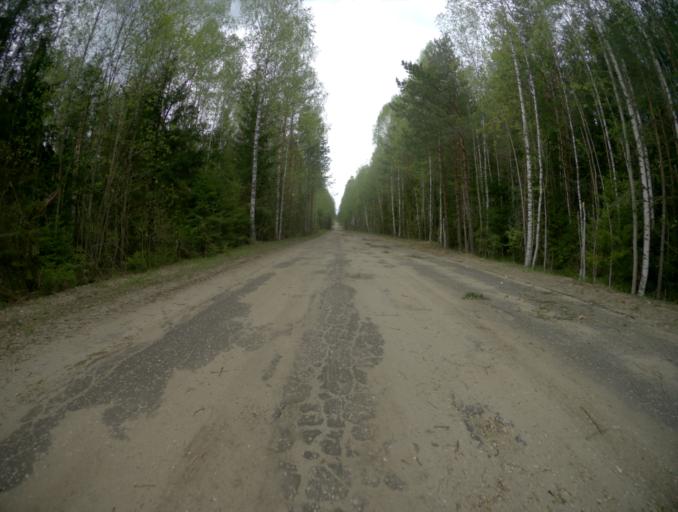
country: RU
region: Vladimir
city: Velikodvorskiy
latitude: 55.2442
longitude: 40.7221
